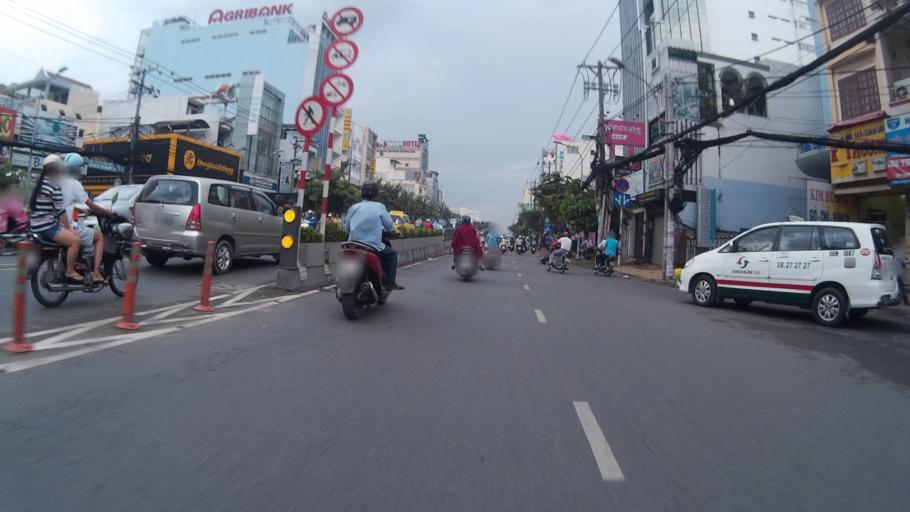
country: VN
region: Ho Chi Minh City
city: Quan Tan Phu
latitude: 10.8019
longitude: 106.6453
